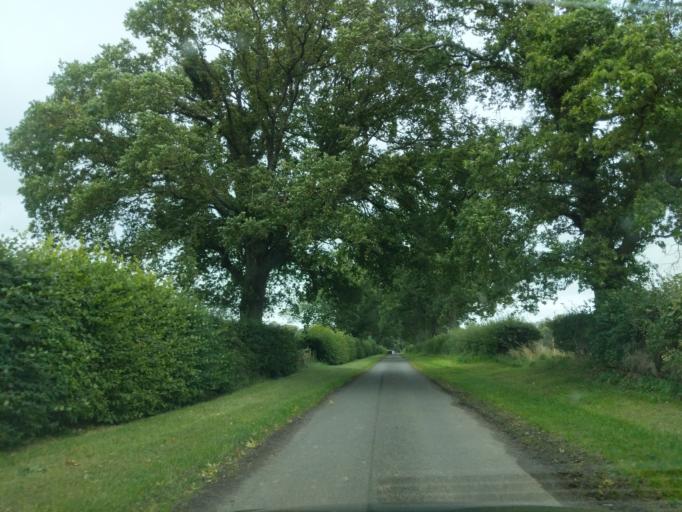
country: GB
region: Scotland
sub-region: The Scottish Borders
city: Kelso
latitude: 55.6187
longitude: -2.4698
